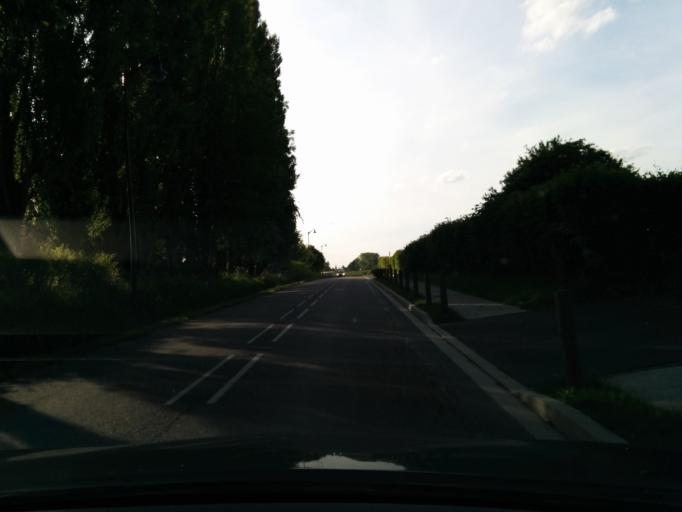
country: FR
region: Haute-Normandie
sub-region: Departement de la Seine-Maritime
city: La Feuillie
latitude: 49.4662
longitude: 1.5151
